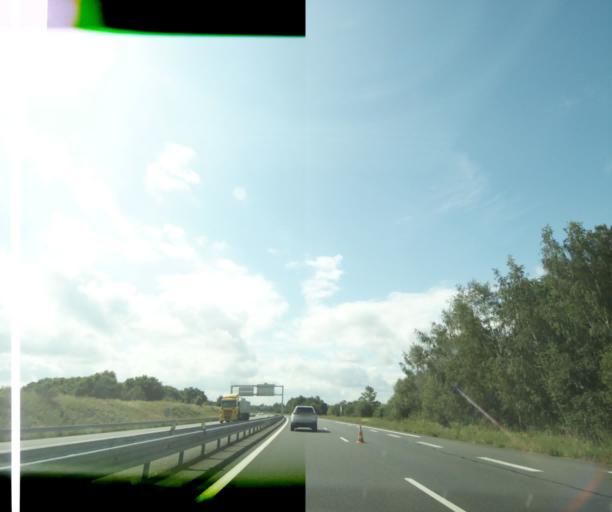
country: FR
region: Pays de la Loire
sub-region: Departement de Maine-et-Loire
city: Jumelles
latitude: 47.4026
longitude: -0.1198
